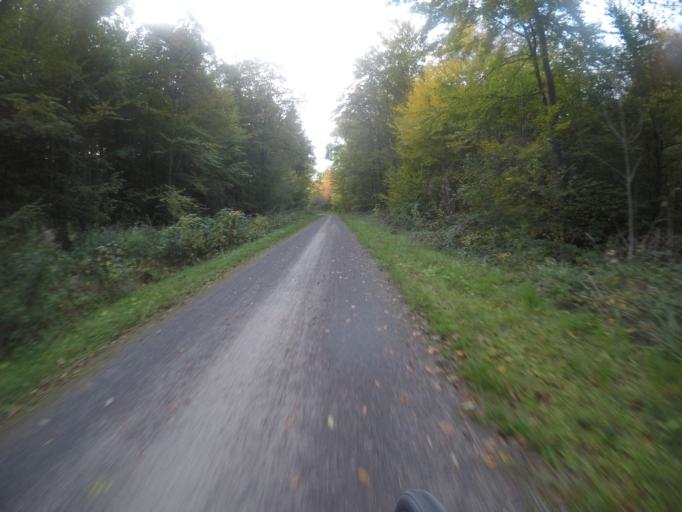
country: DE
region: Baden-Wuerttemberg
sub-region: Regierungsbezirk Stuttgart
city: Weil im Schonbuch
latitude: 48.6121
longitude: 9.0345
